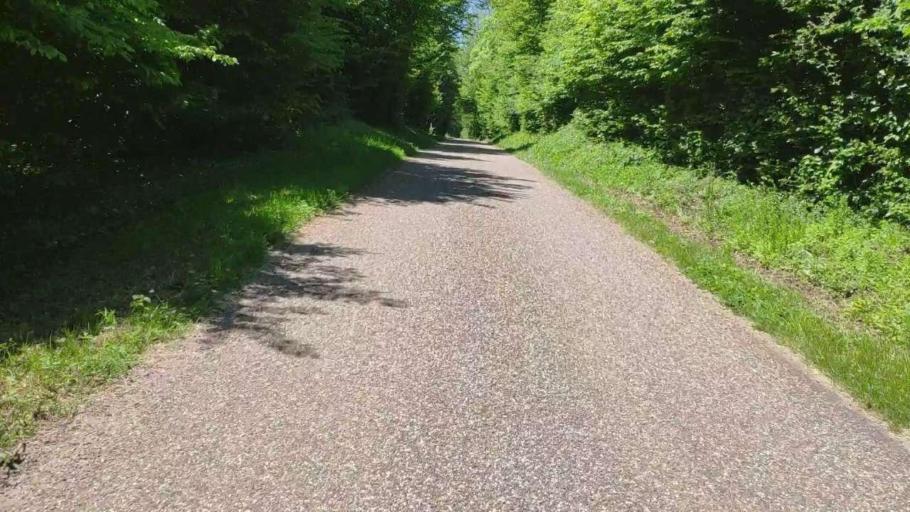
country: FR
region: Franche-Comte
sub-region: Departement du Jura
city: Poligny
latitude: 46.7342
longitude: 5.6755
